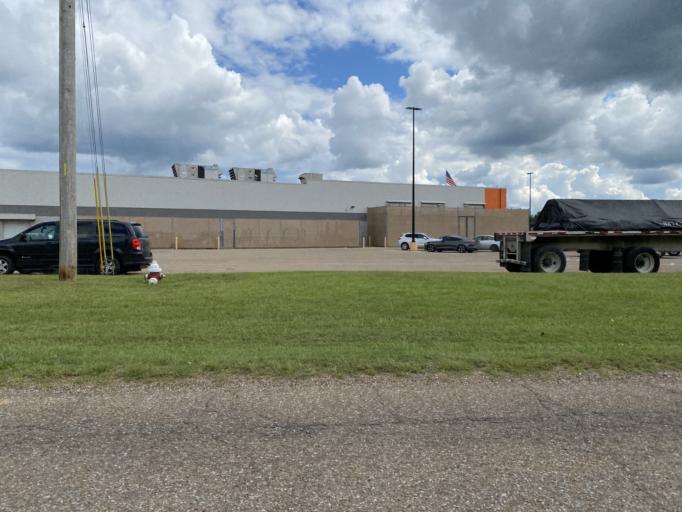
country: US
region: Mississippi
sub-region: Monroe County
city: Amory
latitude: 33.9696
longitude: -88.4579
